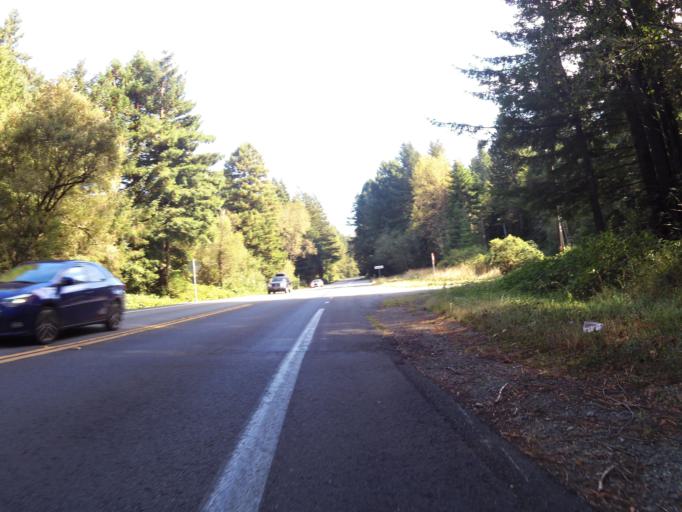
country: US
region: California
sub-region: Del Norte County
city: Bertsch-Oceanview
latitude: 41.8403
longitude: -124.1093
